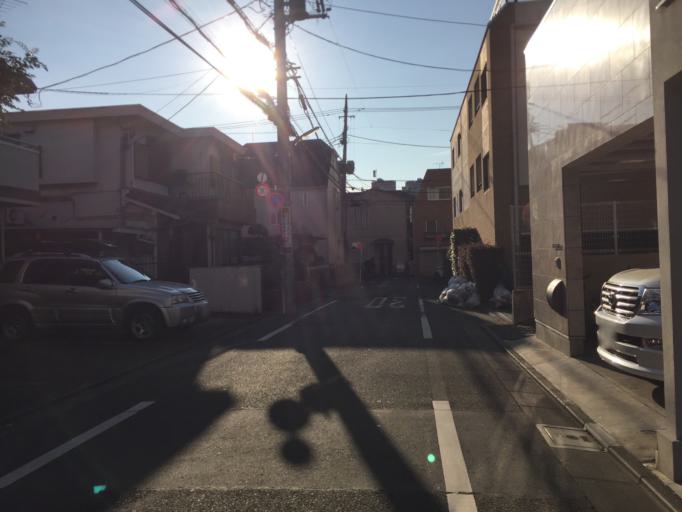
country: JP
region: Tokyo
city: Tokyo
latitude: 35.6521
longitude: 139.6776
